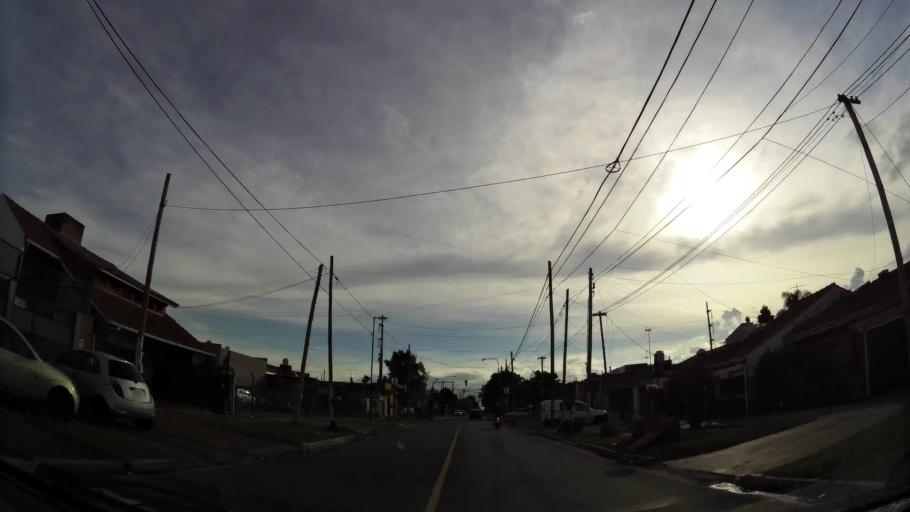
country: AR
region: Buenos Aires
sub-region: Partido de Quilmes
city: Quilmes
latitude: -34.7432
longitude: -58.2721
